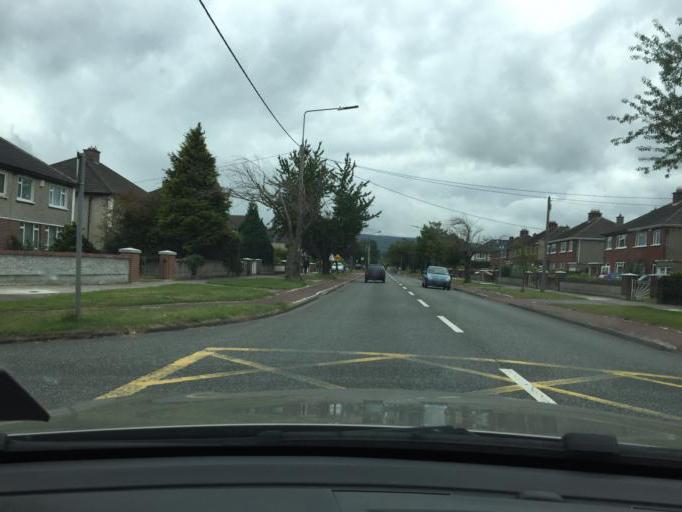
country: IE
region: Leinster
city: Templeogue
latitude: 53.3006
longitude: -6.3097
